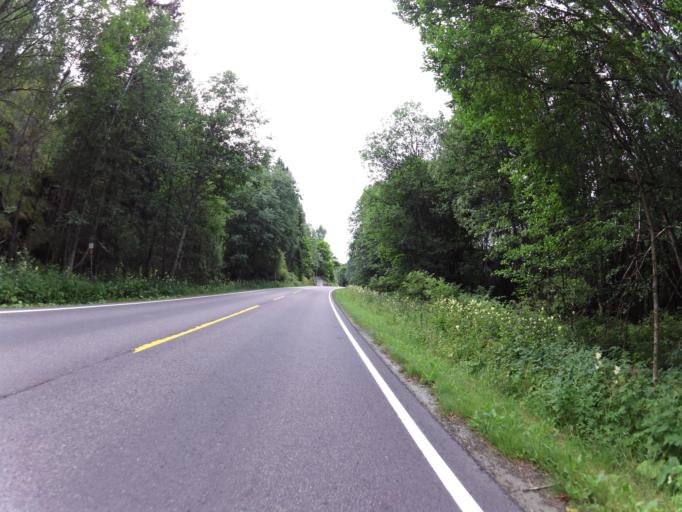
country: NO
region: Akershus
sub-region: Oppegard
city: Kolbotn
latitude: 59.8226
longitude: 10.7728
